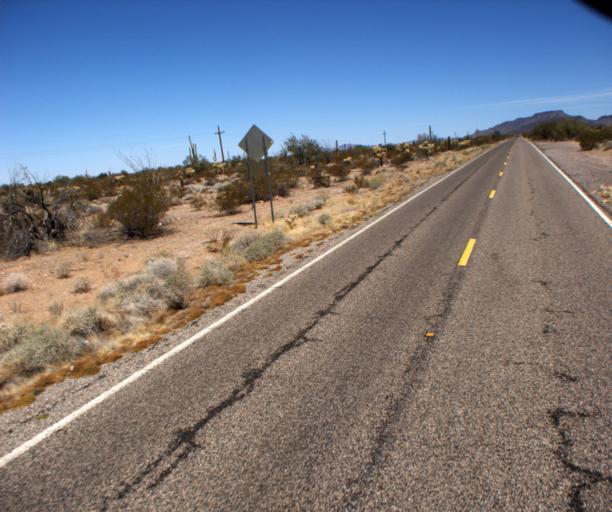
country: US
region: Arizona
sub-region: Pima County
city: Ajo
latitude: 32.2279
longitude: -112.7546
